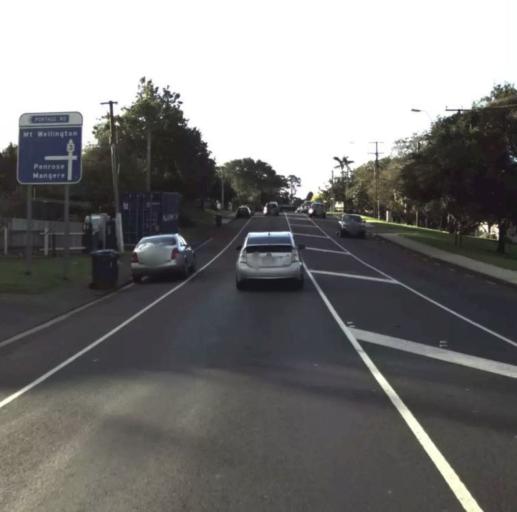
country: NZ
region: Auckland
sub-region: Auckland
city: Tamaki
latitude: -36.9374
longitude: 174.8427
